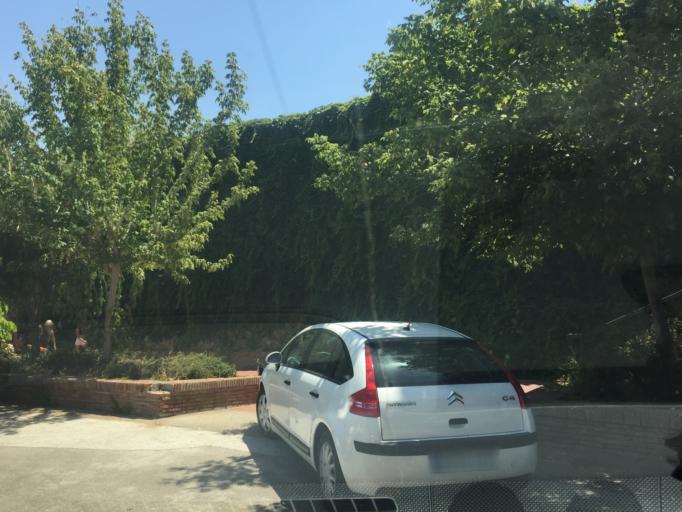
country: ES
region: Andalusia
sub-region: Provincia de Malaga
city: Nerja
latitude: 36.7569
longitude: -3.8426
